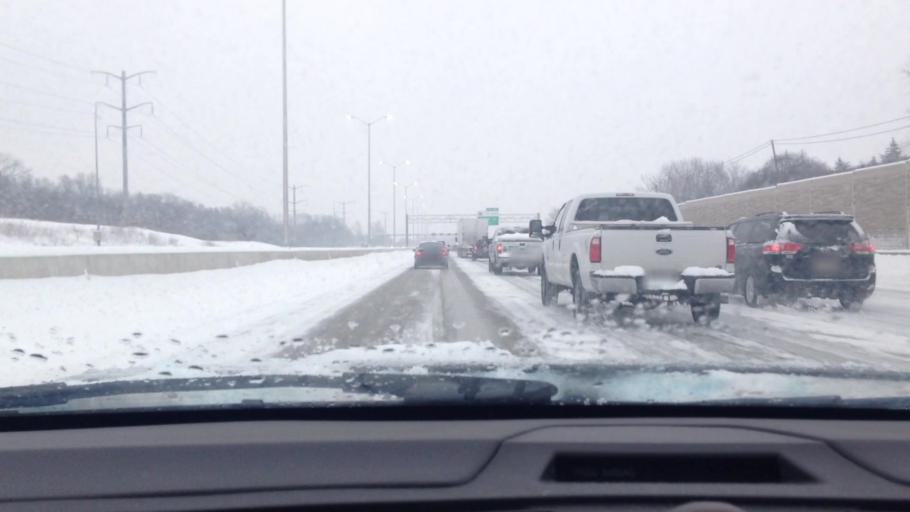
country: US
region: Illinois
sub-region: Cook County
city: South Barrington
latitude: 42.0645
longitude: -88.1126
